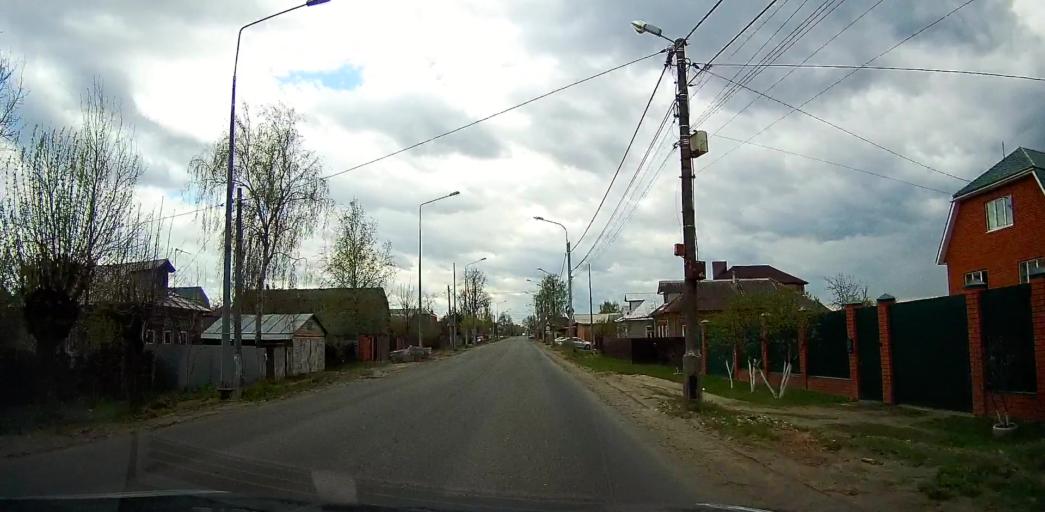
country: RU
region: Moskovskaya
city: Pavlovskiy Posad
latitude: 55.7951
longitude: 38.6883
